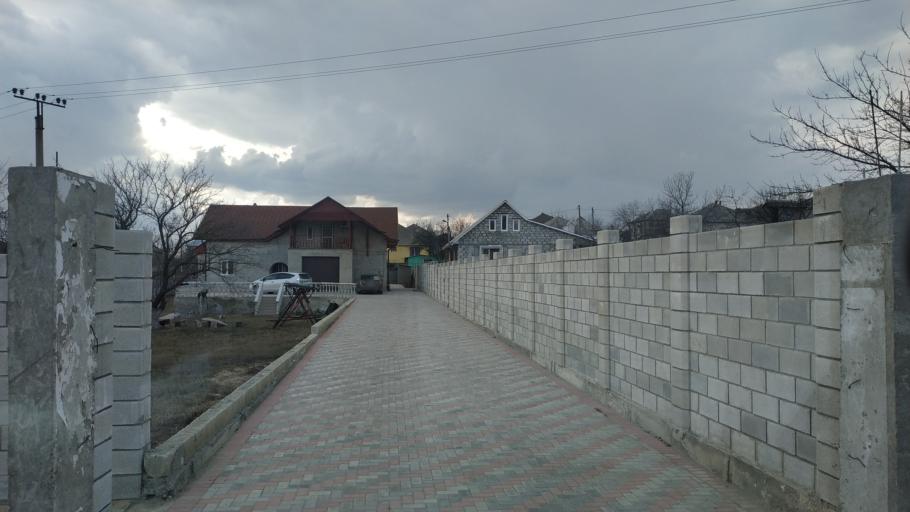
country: MD
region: Anenii Noi
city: Anenii Noi
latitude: 46.8937
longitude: 29.2794
